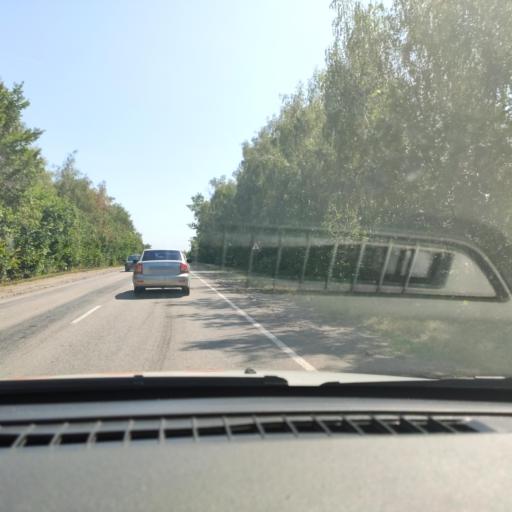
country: RU
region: Voronezj
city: Liski
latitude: 50.7990
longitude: 39.3490
